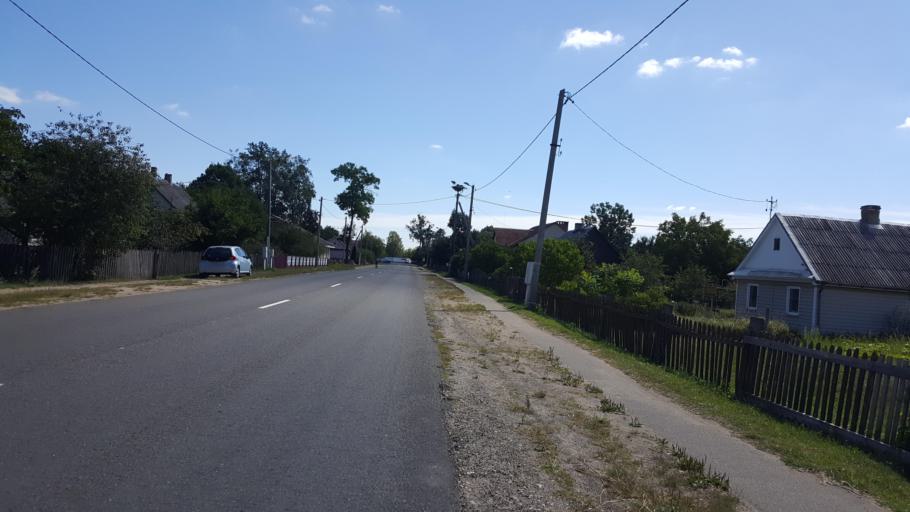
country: BY
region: Brest
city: Kobryn
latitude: 52.3417
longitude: 24.2320
